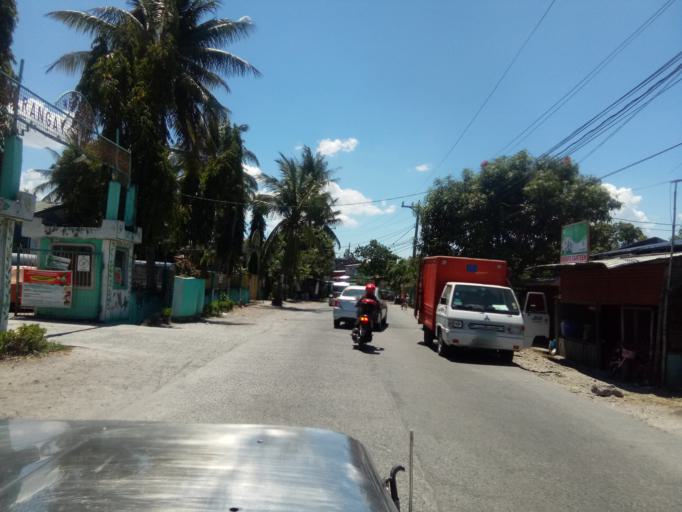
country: PH
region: Calabarzon
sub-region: Province of Cavite
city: Dasmarinas
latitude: 14.3243
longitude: 120.9693
